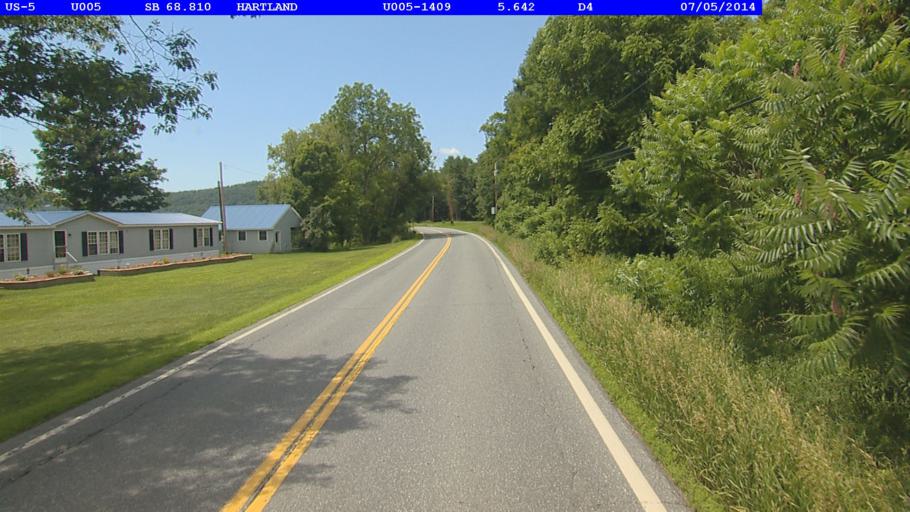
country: US
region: Vermont
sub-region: Windsor County
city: White River Junction
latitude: 43.5866
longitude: -72.3656
